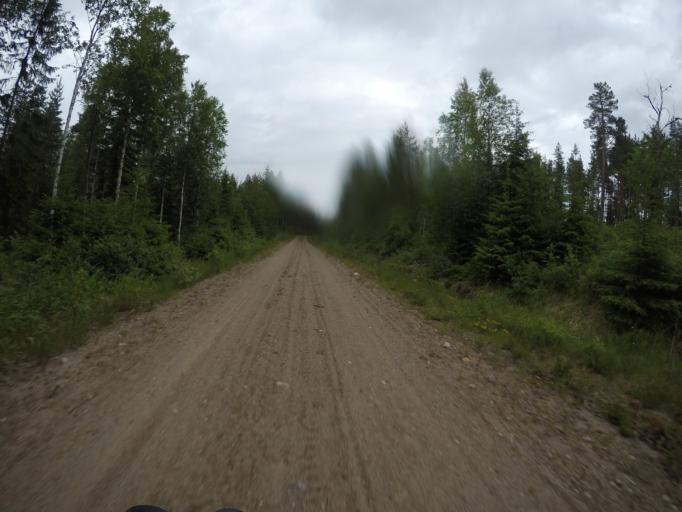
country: SE
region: Dalarna
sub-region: Ludvika Kommun
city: Abborrberget
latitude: 60.0505
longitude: 14.5849
